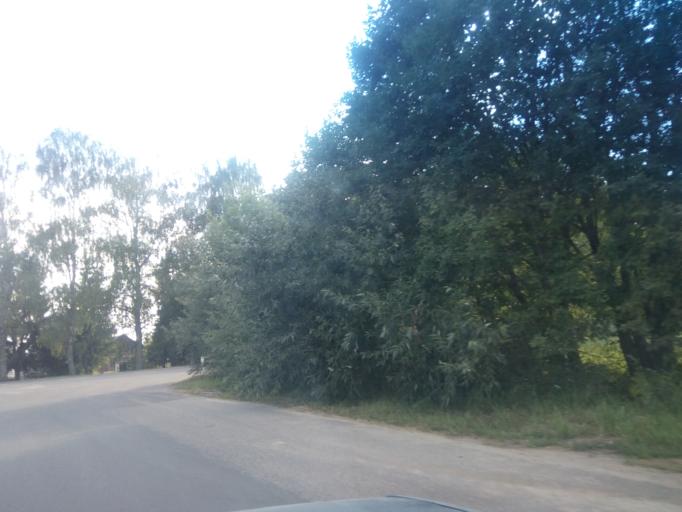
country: BY
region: Vitebsk
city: Navapolatsk
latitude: 55.5428
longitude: 28.6648
